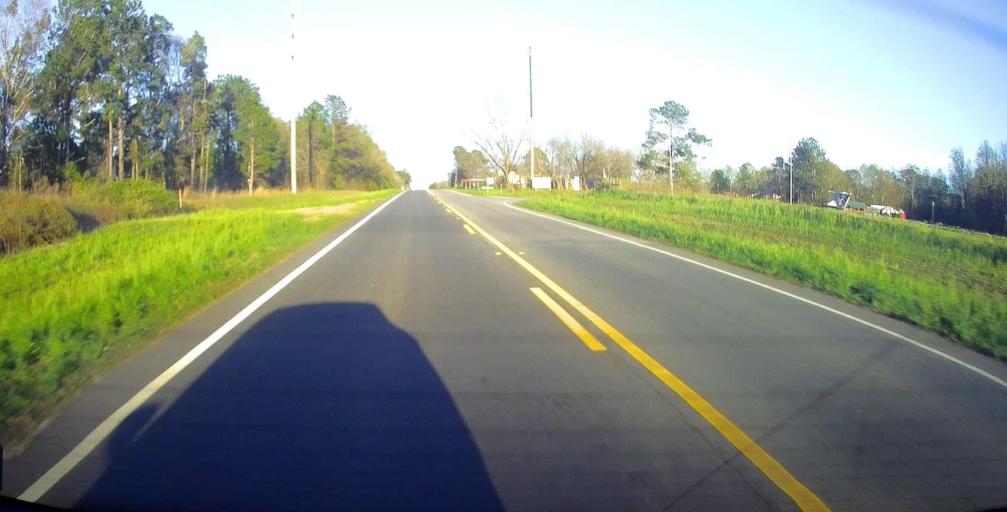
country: US
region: Georgia
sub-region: Wilcox County
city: Rochelle
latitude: 31.9506
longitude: -83.4676
